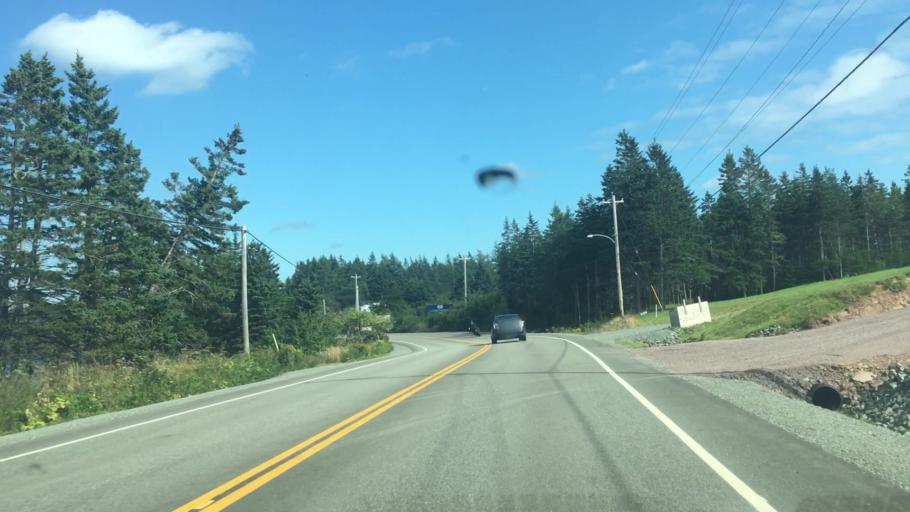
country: CA
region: Nova Scotia
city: Princeville
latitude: 45.6508
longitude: -60.8528
